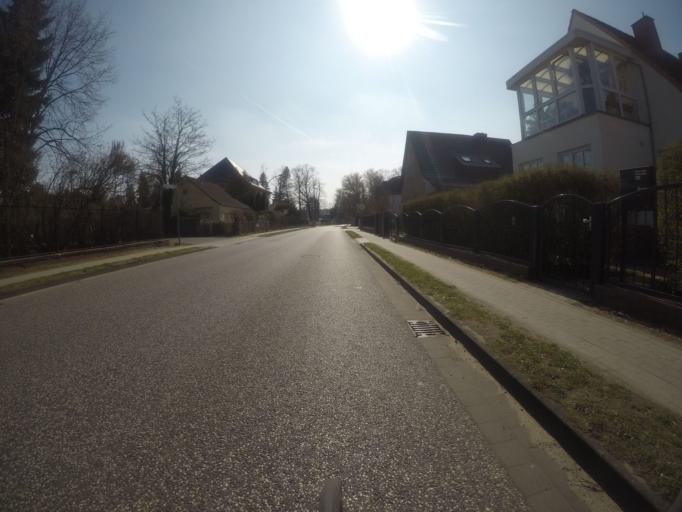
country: DE
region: Brandenburg
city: Konigs Wusterhausen
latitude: 52.3014
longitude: 13.6508
